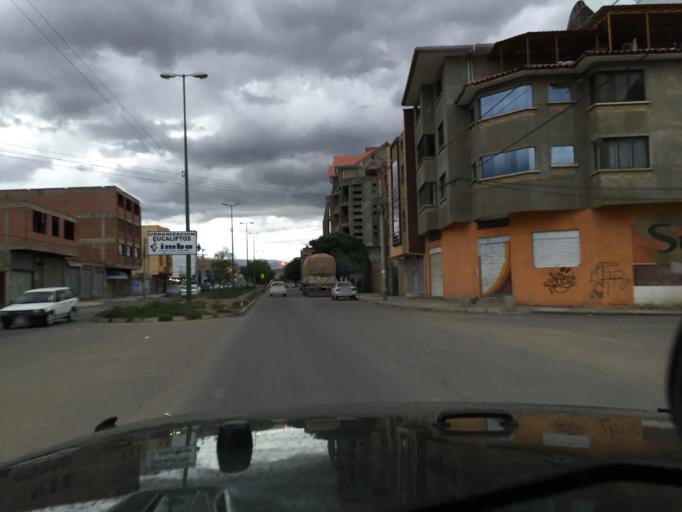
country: BO
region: Cochabamba
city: Cochabamba
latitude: -17.3972
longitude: -66.1993
